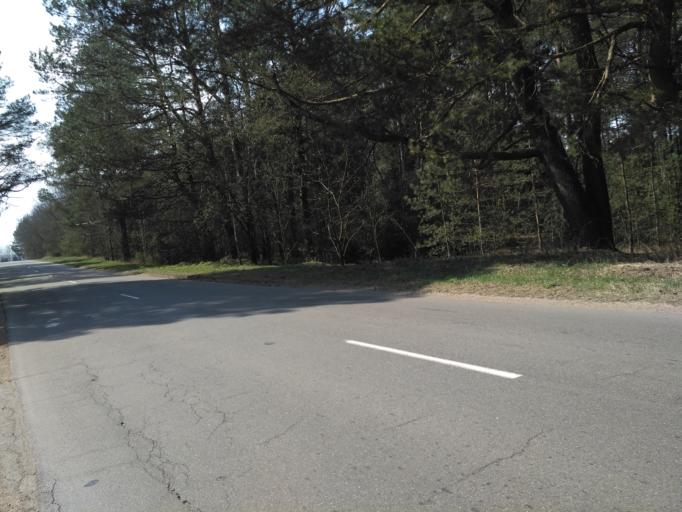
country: BY
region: Minsk
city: Zamostochcha
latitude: 53.8970
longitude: 27.9283
